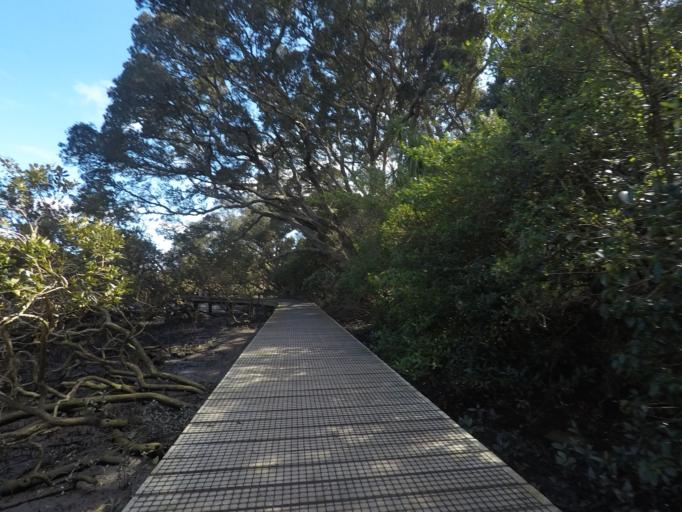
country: NZ
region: Auckland
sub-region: Auckland
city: Rosebank
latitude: -36.8575
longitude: 174.7133
